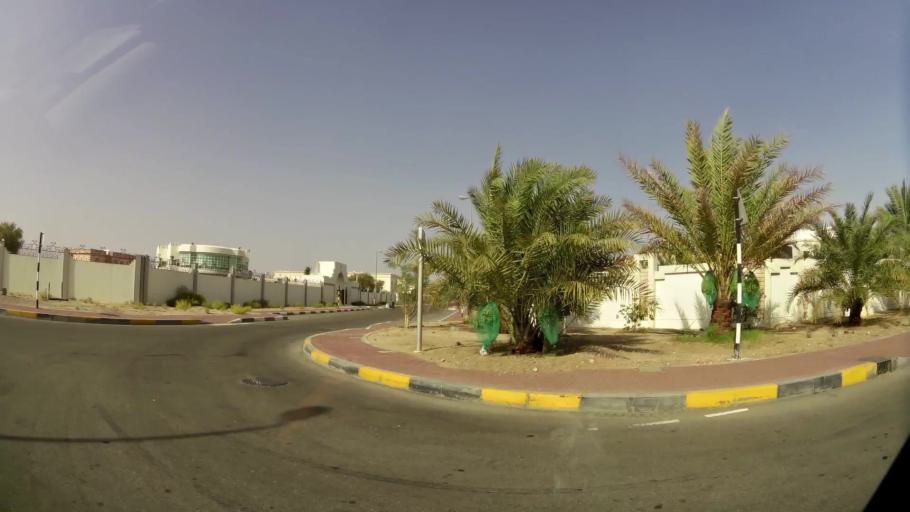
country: AE
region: Abu Dhabi
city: Al Ain
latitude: 24.2359
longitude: 55.6704
